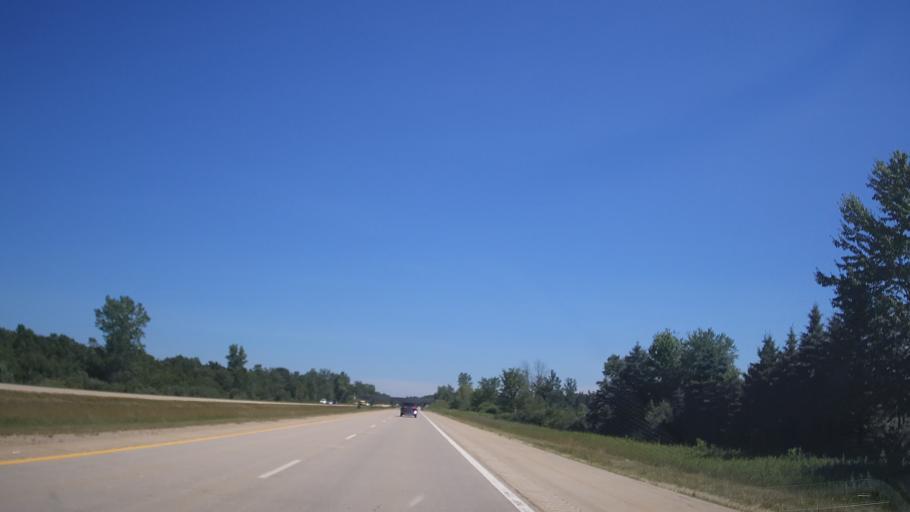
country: US
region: Michigan
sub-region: Midland County
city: Coleman
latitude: 43.7606
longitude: -84.5562
